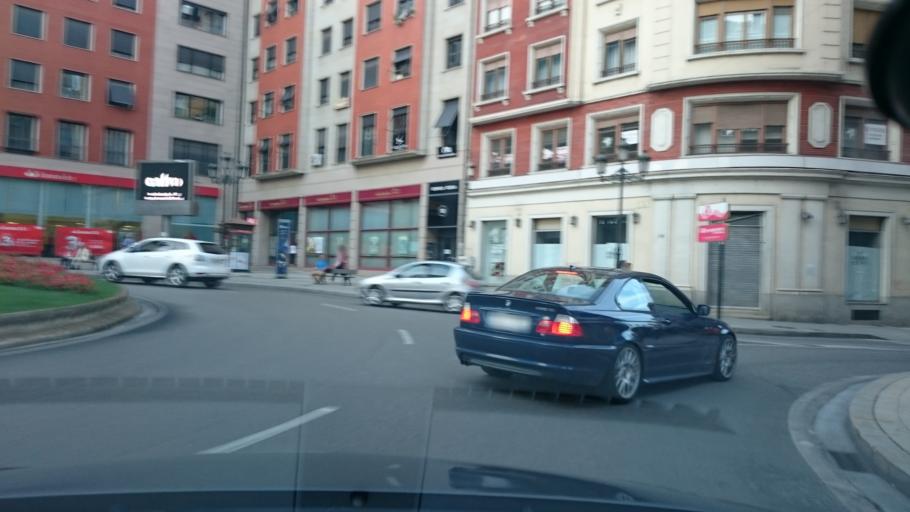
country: ES
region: Castille and Leon
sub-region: Provincia de Leon
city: Ponferrada
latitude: 42.5478
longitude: -6.5980
